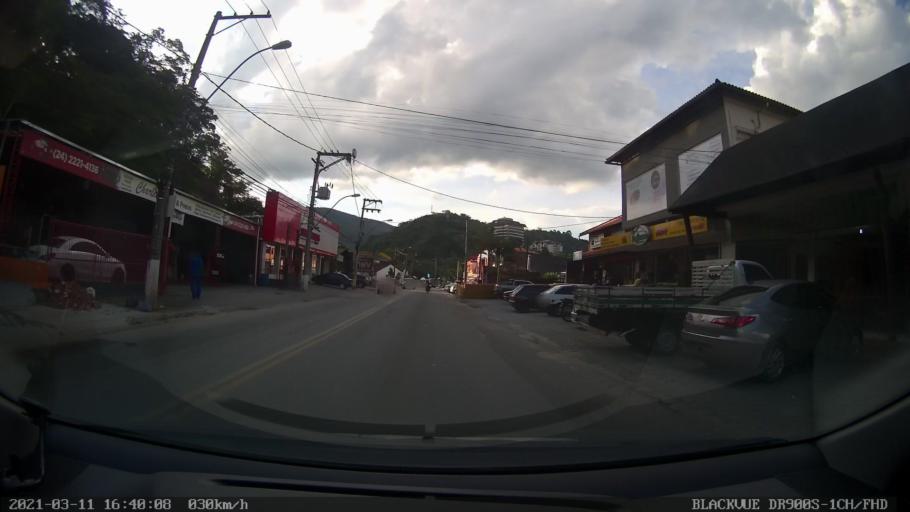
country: BR
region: Rio de Janeiro
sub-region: Petropolis
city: Petropolis
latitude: -22.4161
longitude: -43.1390
